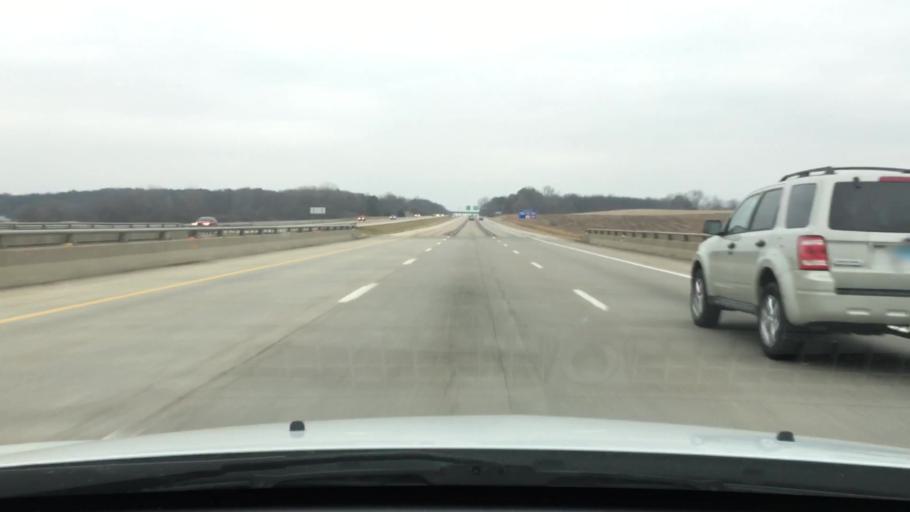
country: US
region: Illinois
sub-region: Logan County
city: Lincoln
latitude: 40.1348
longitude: -89.4169
